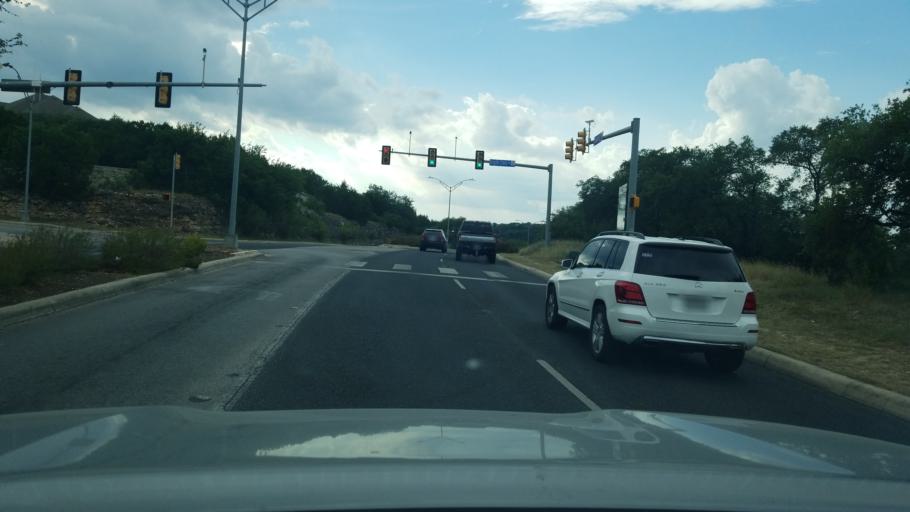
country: US
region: Texas
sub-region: Bexar County
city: Hollywood Park
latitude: 29.6394
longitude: -98.4790
